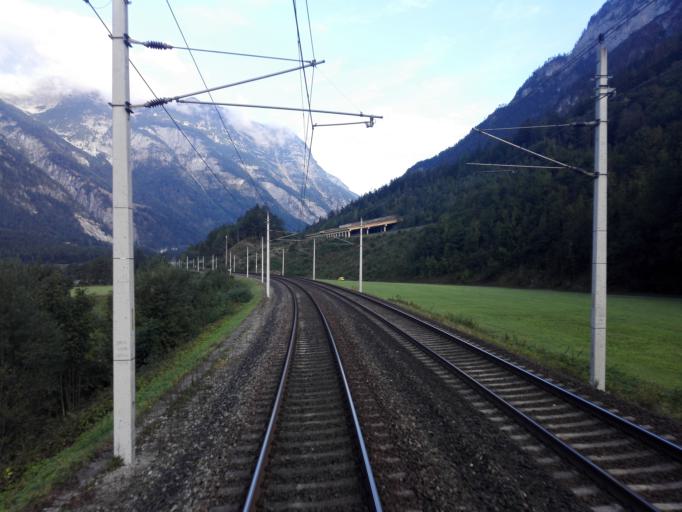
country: AT
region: Salzburg
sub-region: Politischer Bezirk Sankt Johann im Pongau
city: Werfen
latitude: 47.5021
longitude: 13.1770
